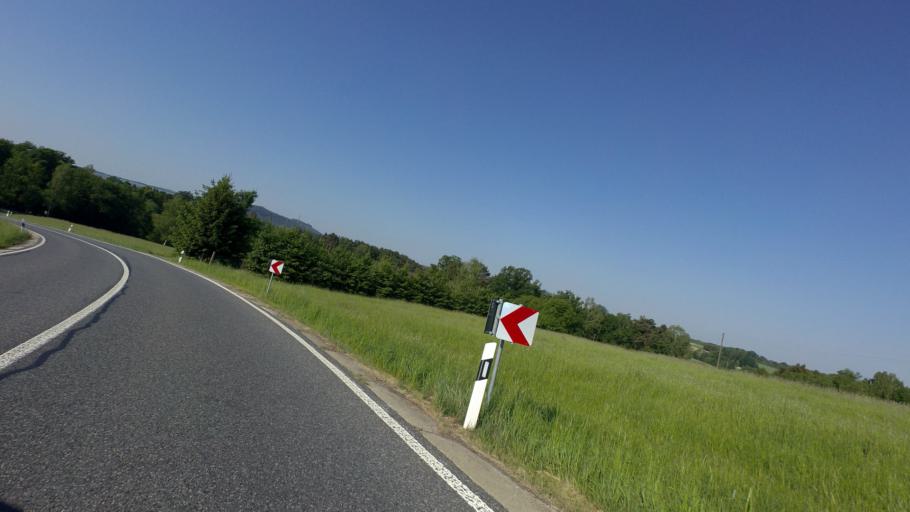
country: DE
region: Saxony
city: Bad Schandau
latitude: 50.9292
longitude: 14.1650
